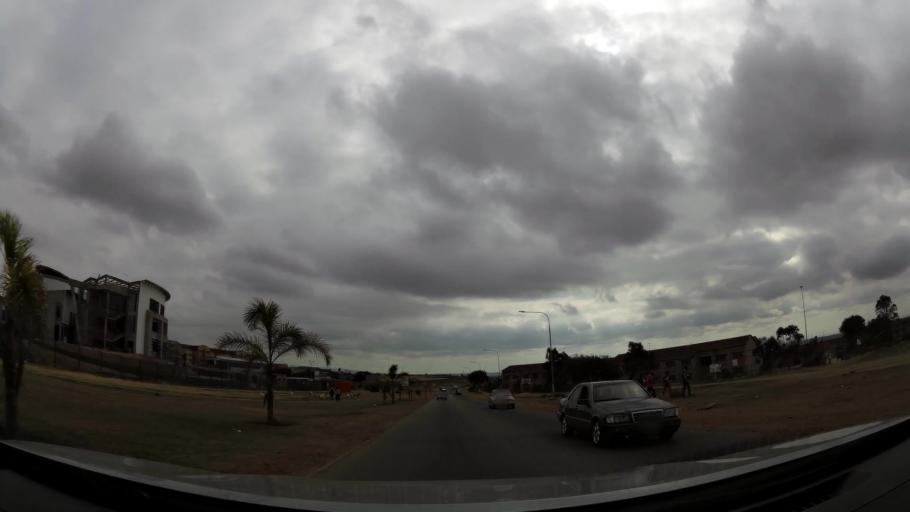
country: ZA
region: Eastern Cape
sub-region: Nelson Mandela Bay Metropolitan Municipality
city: Port Elizabeth
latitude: -33.8798
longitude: 25.5636
